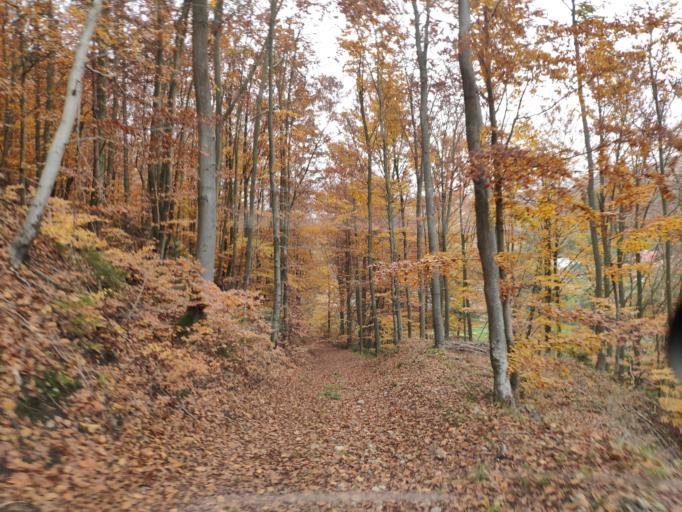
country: SK
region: Kosicky
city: Moldava nad Bodvou
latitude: 48.7413
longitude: 21.0182
